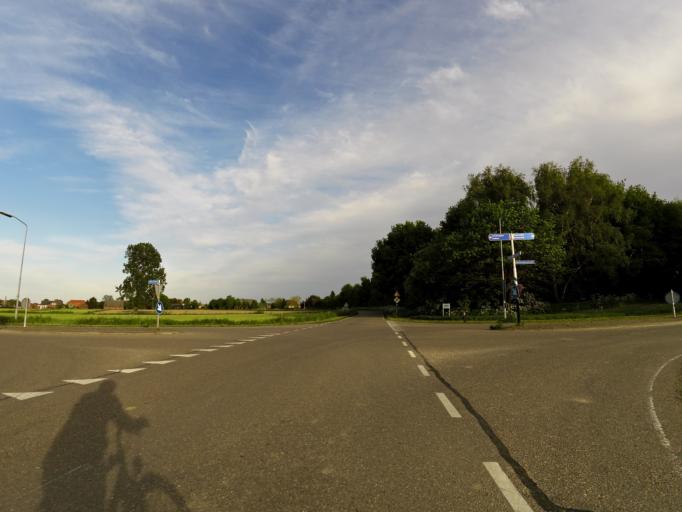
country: NL
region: Gelderland
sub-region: Oude IJsselstreek
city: Gendringen
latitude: 51.8705
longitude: 6.3502
